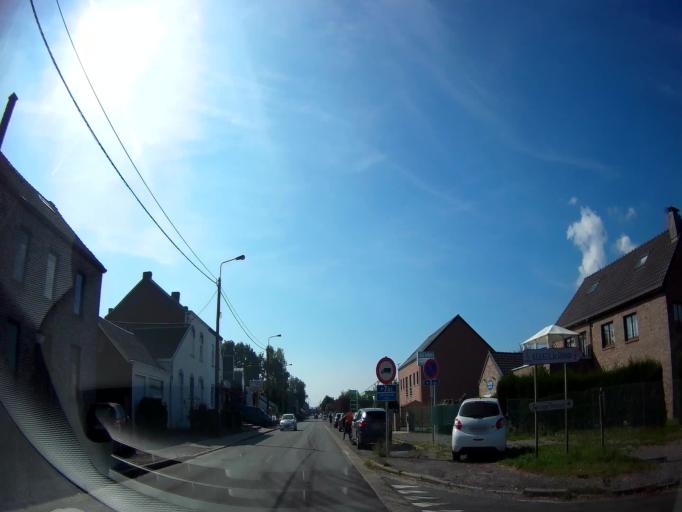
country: BE
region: Wallonia
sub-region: Province de Liege
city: Amay
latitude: 50.5582
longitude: 5.3057
